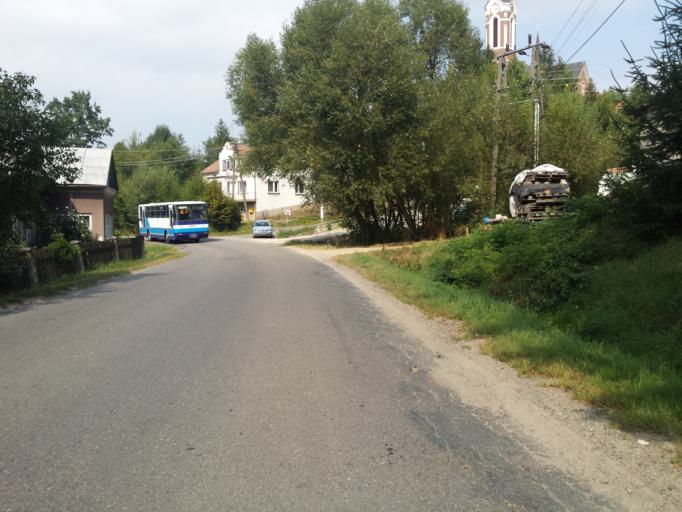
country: PL
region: Subcarpathian Voivodeship
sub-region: Powiat rzeszowski
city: Blazowa
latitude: 49.8592
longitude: 22.1317
